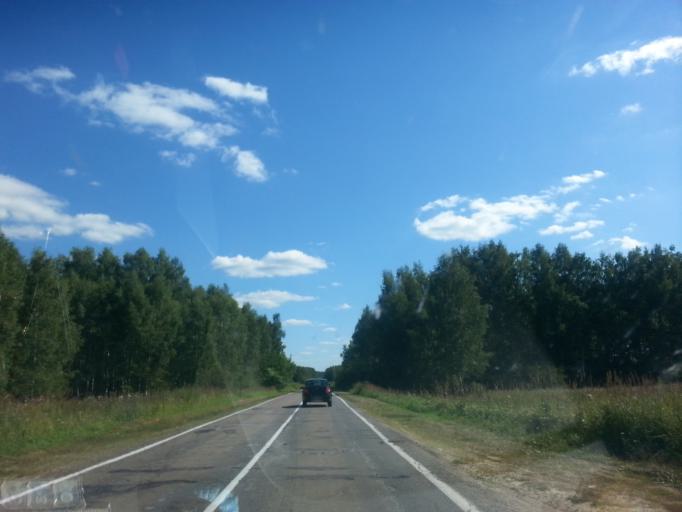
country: RU
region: Vladimir
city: Galitsy
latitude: 56.1514
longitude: 42.8592
